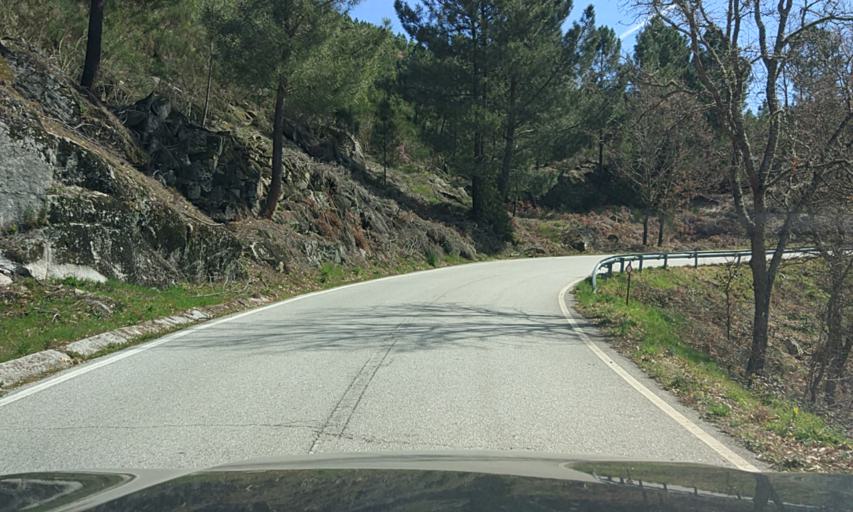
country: PT
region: Vila Real
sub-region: Sabrosa
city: Sabrosa
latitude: 41.3372
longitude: -7.5801
